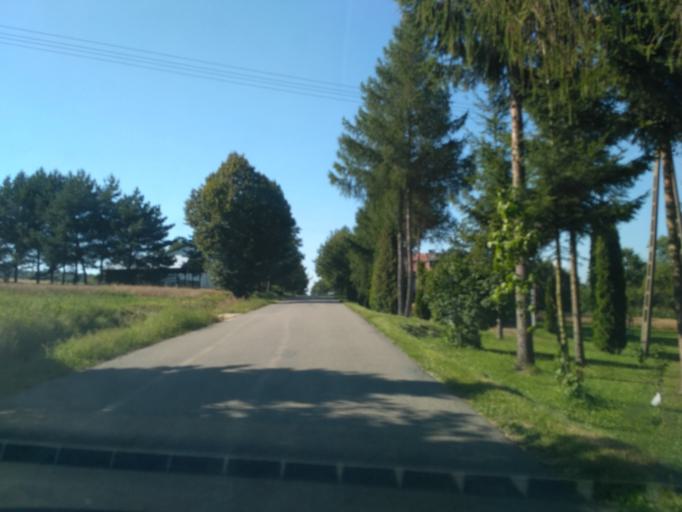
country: PL
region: Subcarpathian Voivodeship
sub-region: Powiat strzyzowski
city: Wysoka Strzyzowska
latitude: 49.8083
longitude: 21.7458
